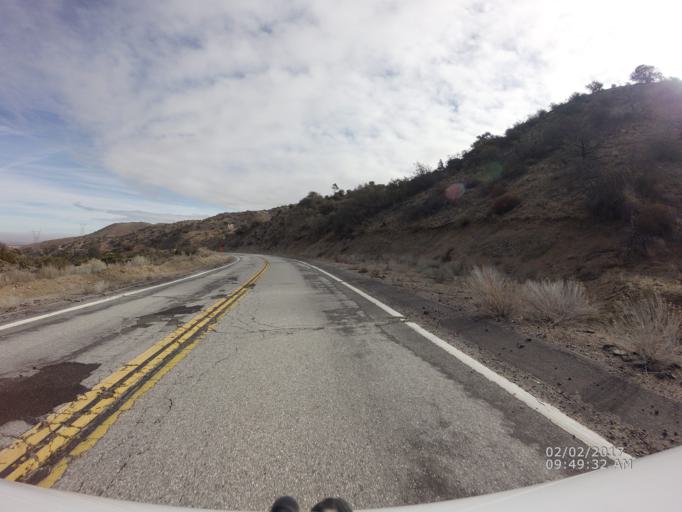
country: US
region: California
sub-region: Los Angeles County
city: Vincent
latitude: 34.4813
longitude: -118.0675
